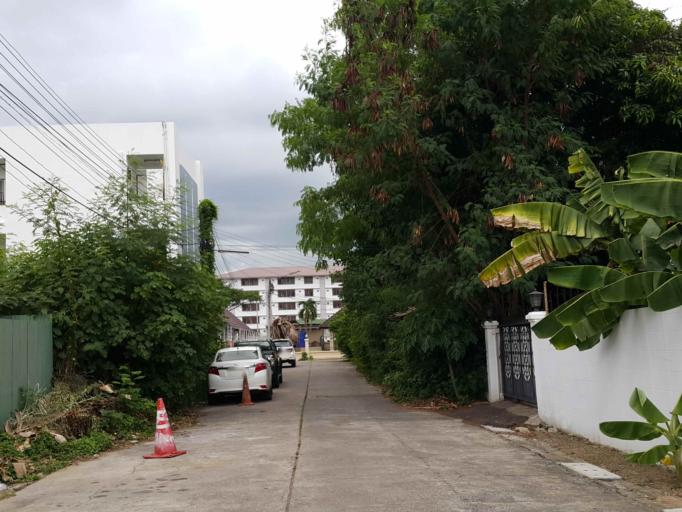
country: TH
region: Chiang Mai
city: Chiang Mai
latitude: 18.7665
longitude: 99.0213
